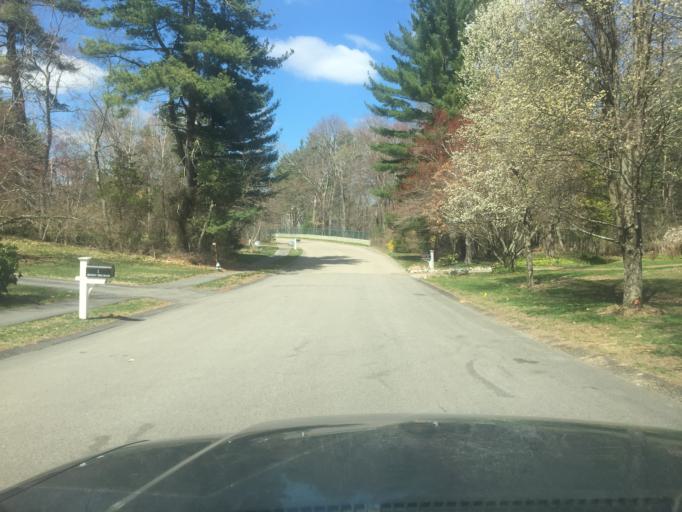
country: US
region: Massachusetts
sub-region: Norfolk County
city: Medway
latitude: 42.1667
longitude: -71.4004
